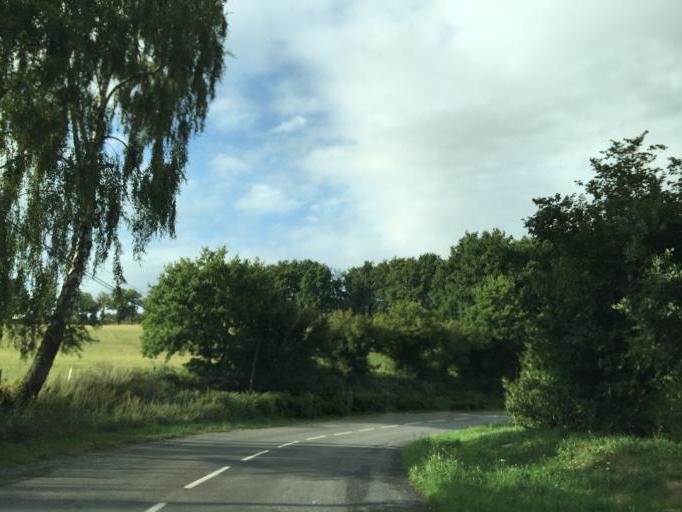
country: FR
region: Midi-Pyrenees
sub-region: Departement de l'Aveyron
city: Pont-de-Salars
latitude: 44.3023
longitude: 2.7316
